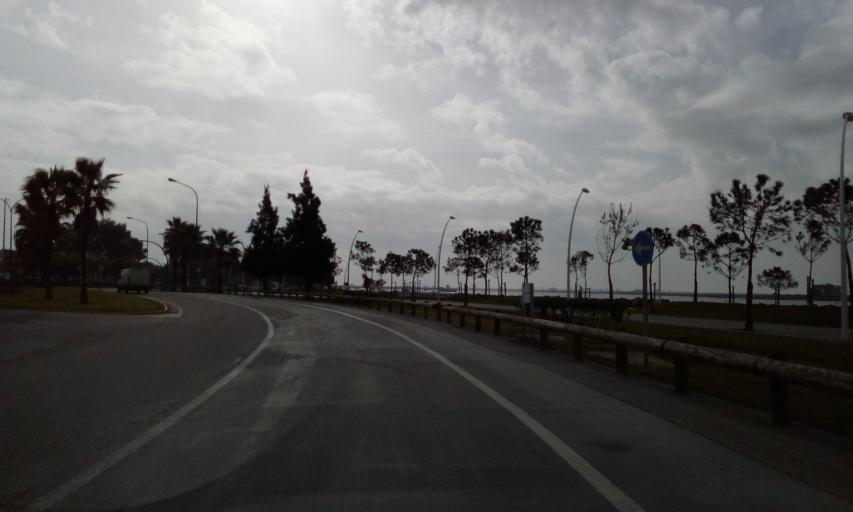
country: ES
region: Andalusia
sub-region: Provincia de Huelva
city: Huelva
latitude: 37.2421
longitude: -6.9552
